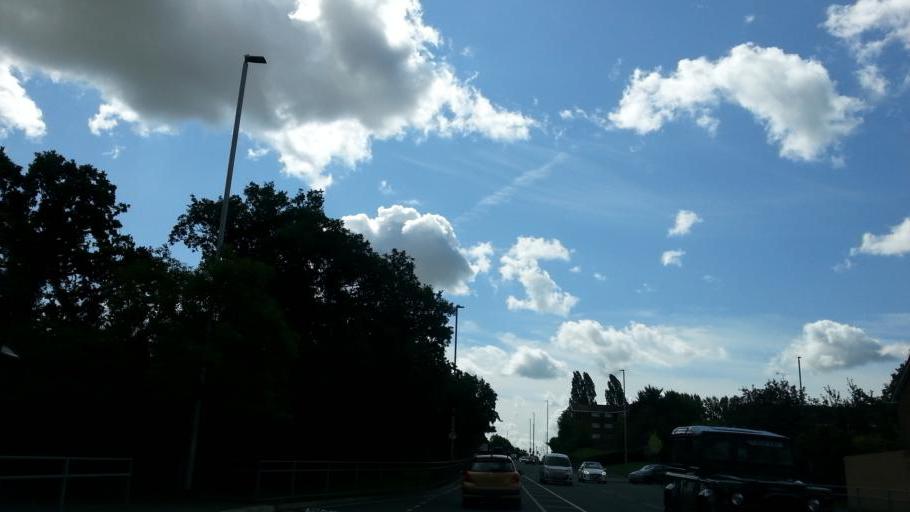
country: GB
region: England
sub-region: Essex
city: Basildon
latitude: 51.5652
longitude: 0.4526
